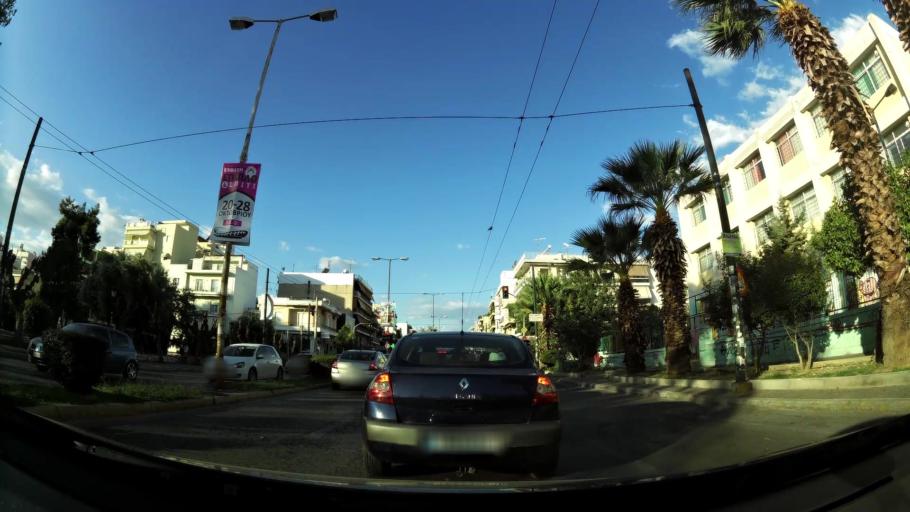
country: GR
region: Attica
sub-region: Nomos Piraios
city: Nikaia
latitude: 37.9723
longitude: 23.6582
